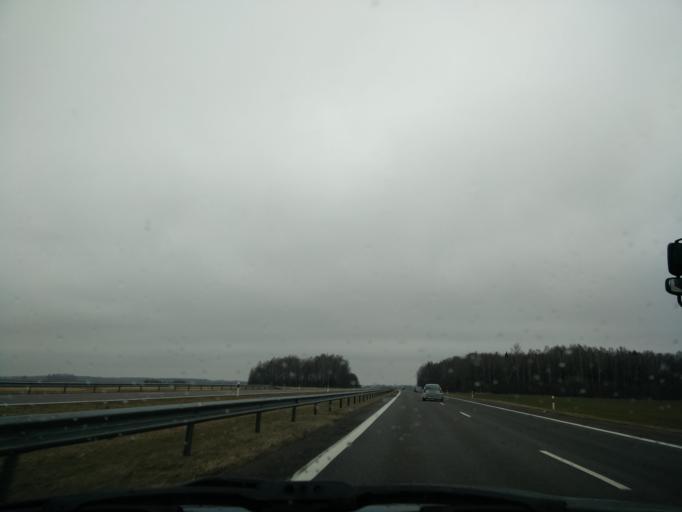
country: LT
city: Raseiniai
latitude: 55.3573
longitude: 23.0294
